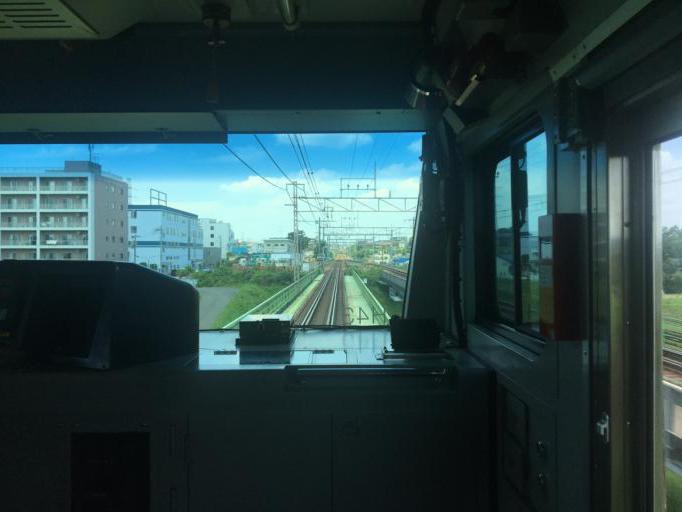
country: JP
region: Tokyo
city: Hino
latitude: 35.6882
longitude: 139.3986
